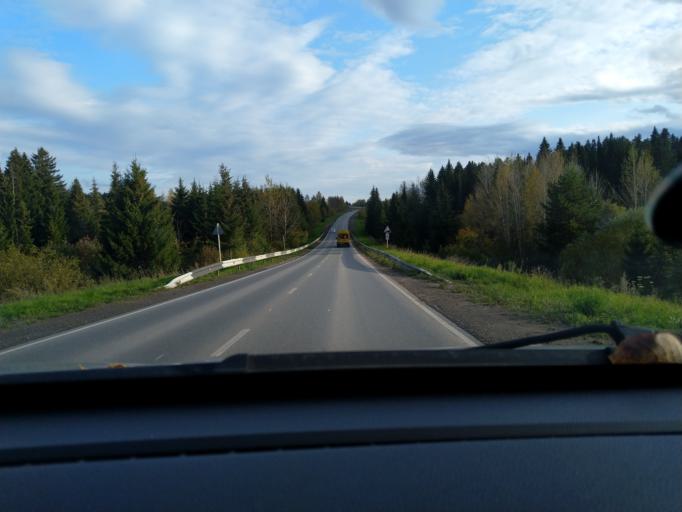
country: RU
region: Perm
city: Polazna
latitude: 58.2804
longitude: 56.4128
